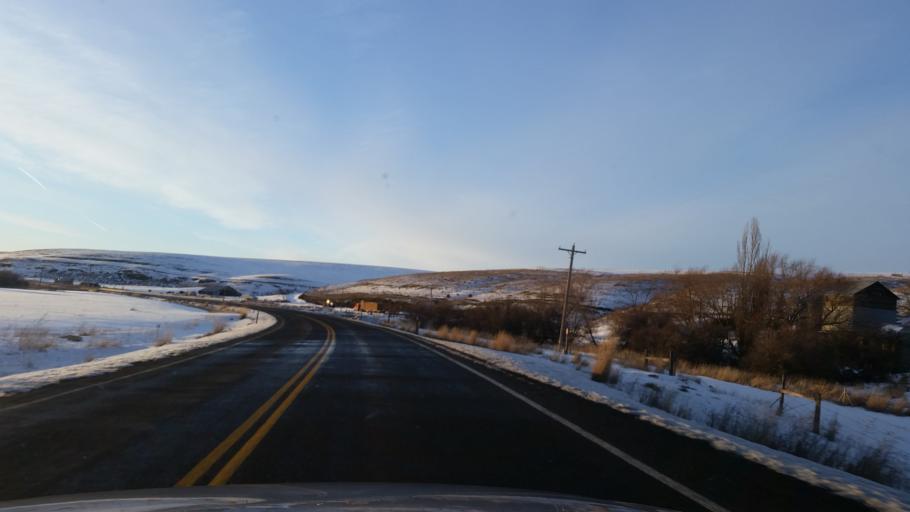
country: US
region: Washington
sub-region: Whitman County
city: Colfax
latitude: 47.1162
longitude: -117.6442
